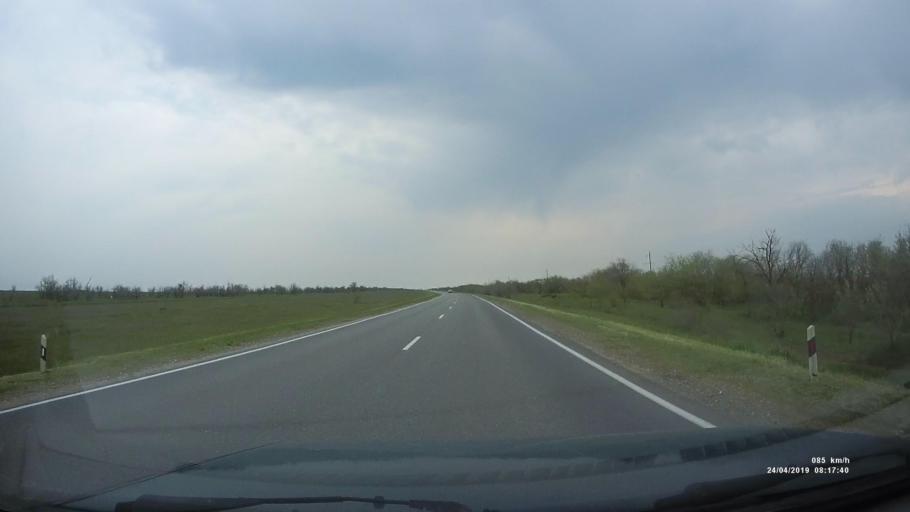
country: RU
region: Kalmykiya
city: Priyutnoye
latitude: 46.0976
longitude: 43.6351
